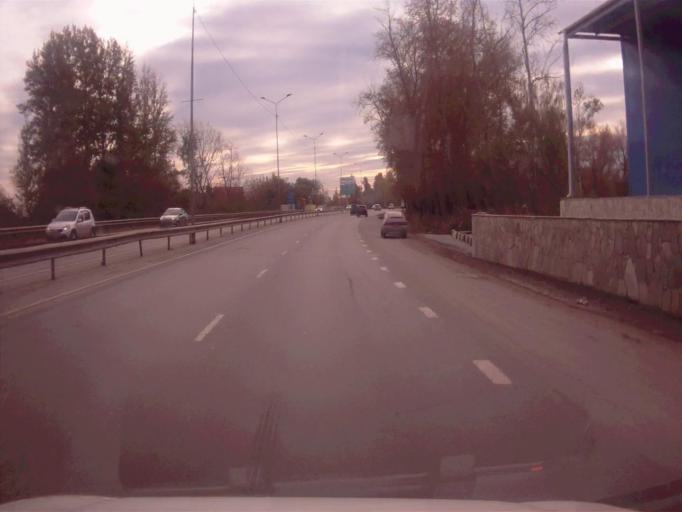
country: RU
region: Chelyabinsk
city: Novosineglazovskiy
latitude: 55.0872
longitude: 61.3983
